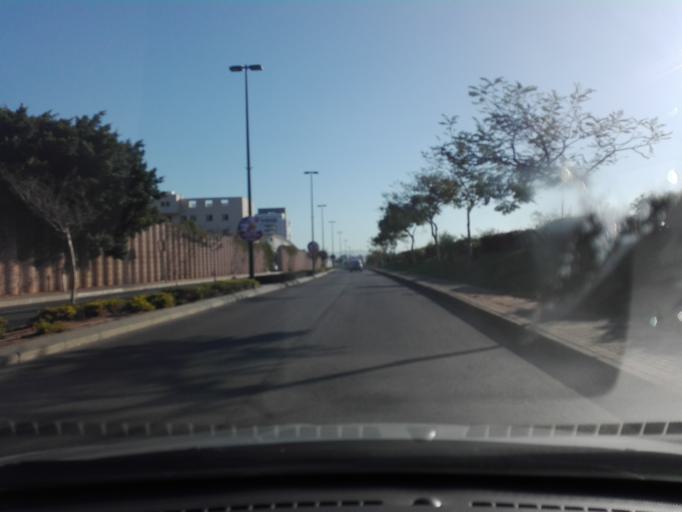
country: IL
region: Central District
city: Netanya
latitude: 32.3086
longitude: 34.8556
